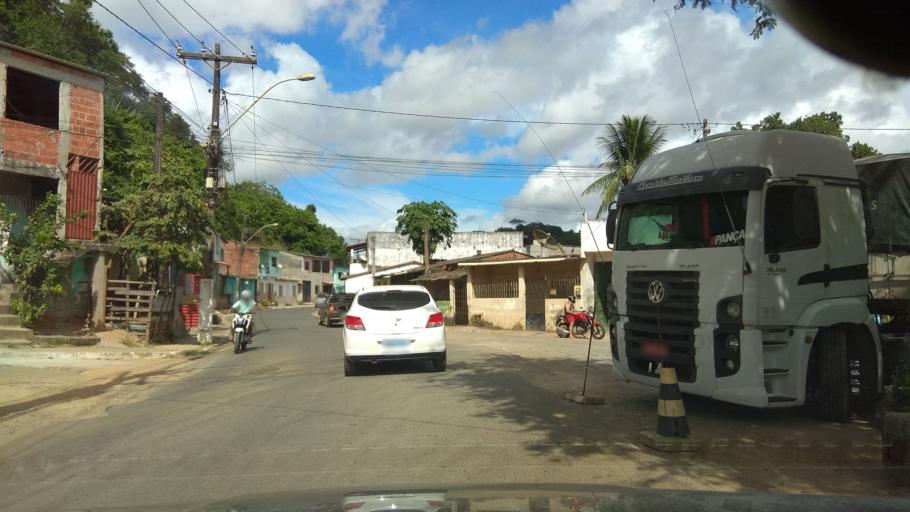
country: BR
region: Bahia
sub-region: Ilheus
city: Ilheus
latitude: -14.7910
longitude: -39.0619
